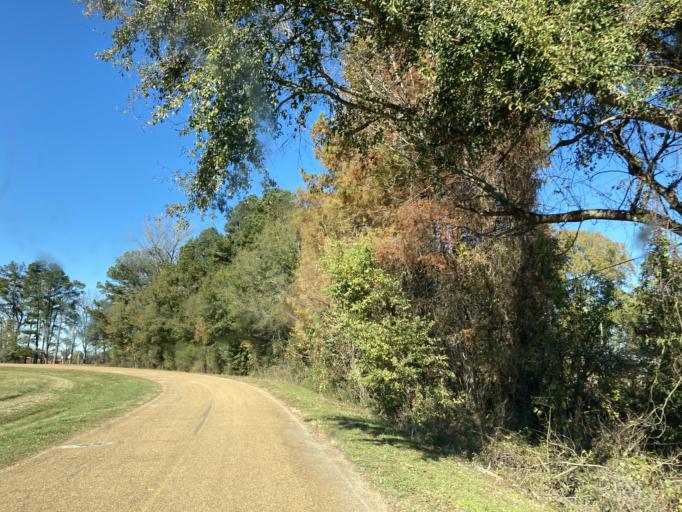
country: US
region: Mississippi
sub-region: Hinds County
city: Lynchburg
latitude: 32.6373
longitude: -90.6049
